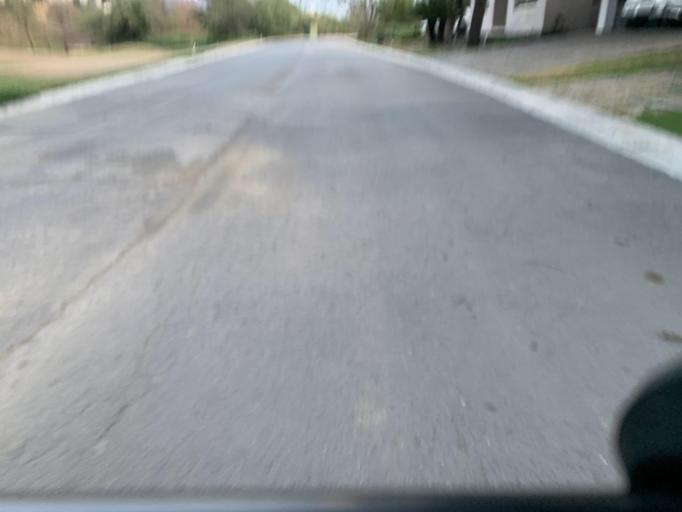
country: MX
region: Nuevo Leon
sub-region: Juarez
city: Bosques de San Pedro
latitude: 25.5202
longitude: -100.1952
